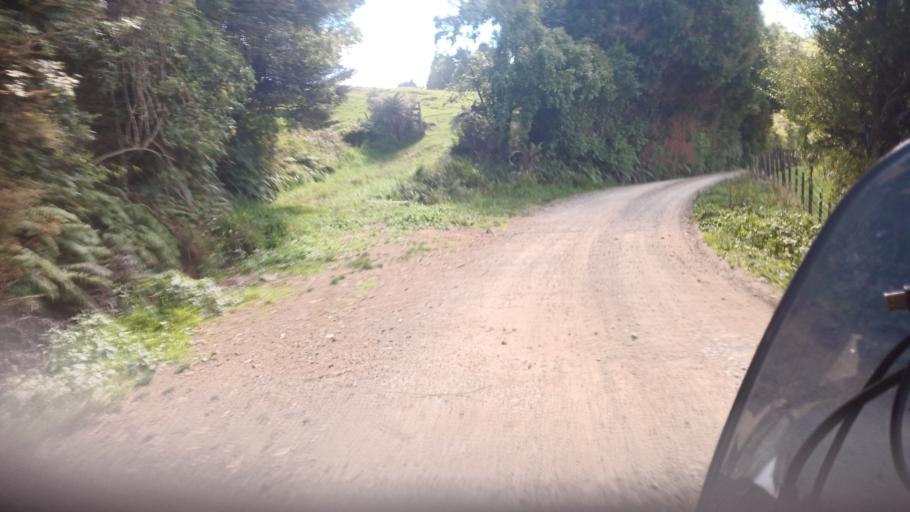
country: NZ
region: Bay of Plenty
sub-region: Opotiki District
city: Opotiki
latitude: -38.3454
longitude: 177.5833
